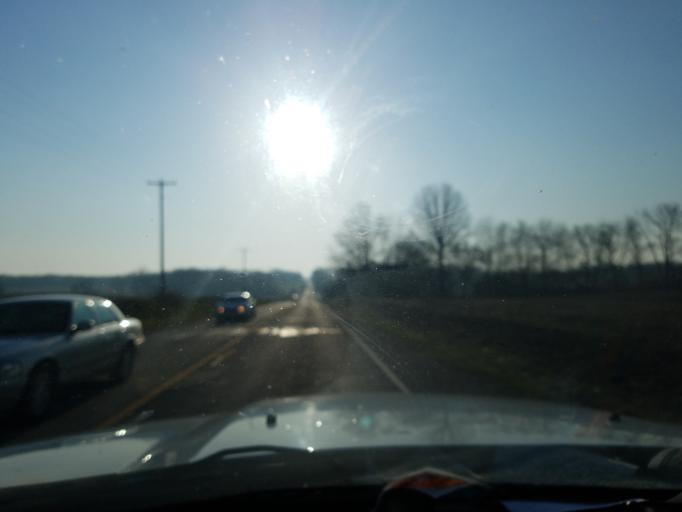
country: US
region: Indiana
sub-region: Vigo County
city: Seelyville
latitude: 39.3901
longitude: -87.2362
